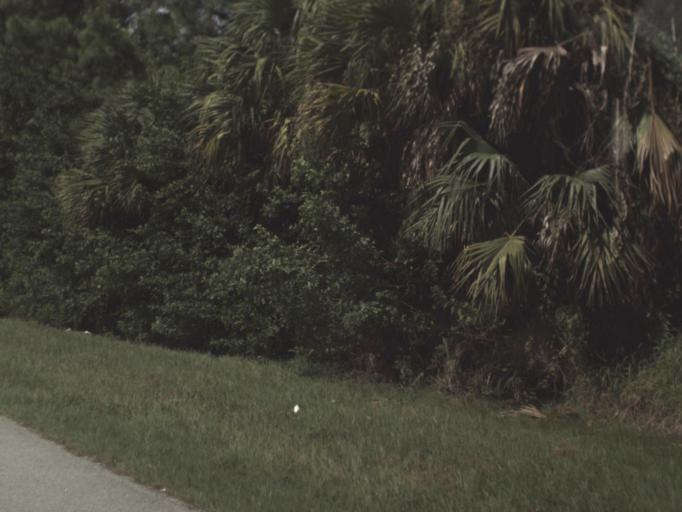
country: US
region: Florida
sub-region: Collier County
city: Immokalee
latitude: 26.5040
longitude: -81.5070
